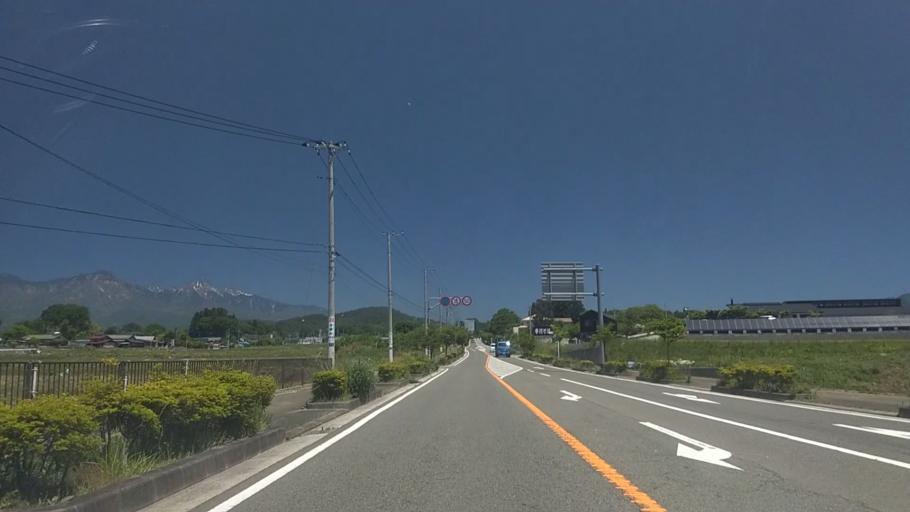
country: JP
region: Yamanashi
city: Nirasaki
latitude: 35.8304
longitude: 138.4297
